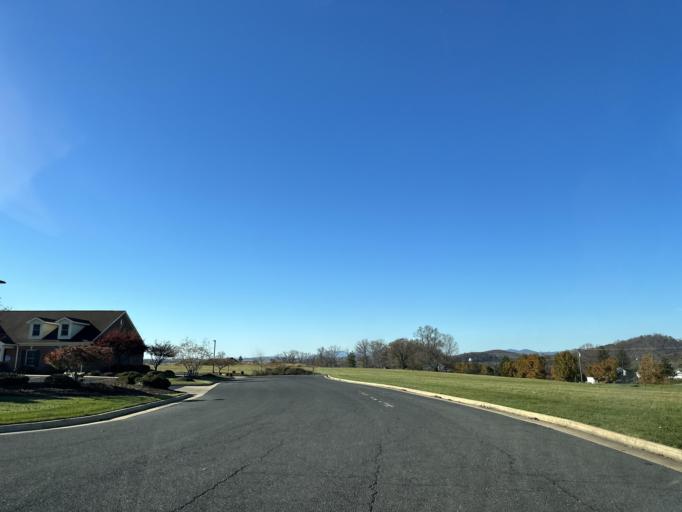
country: US
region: Virginia
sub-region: Rockingham County
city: Bridgewater
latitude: 38.3947
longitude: -78.9579
